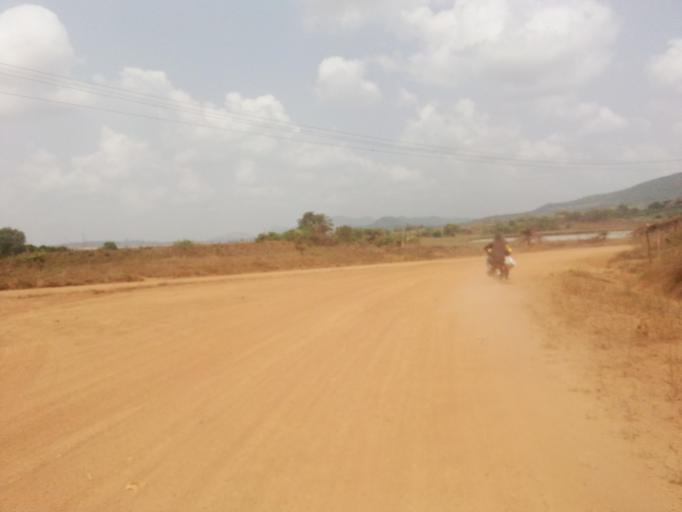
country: SL
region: Southern Province
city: Mogbwemo
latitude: 7.6659
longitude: -12.2789
